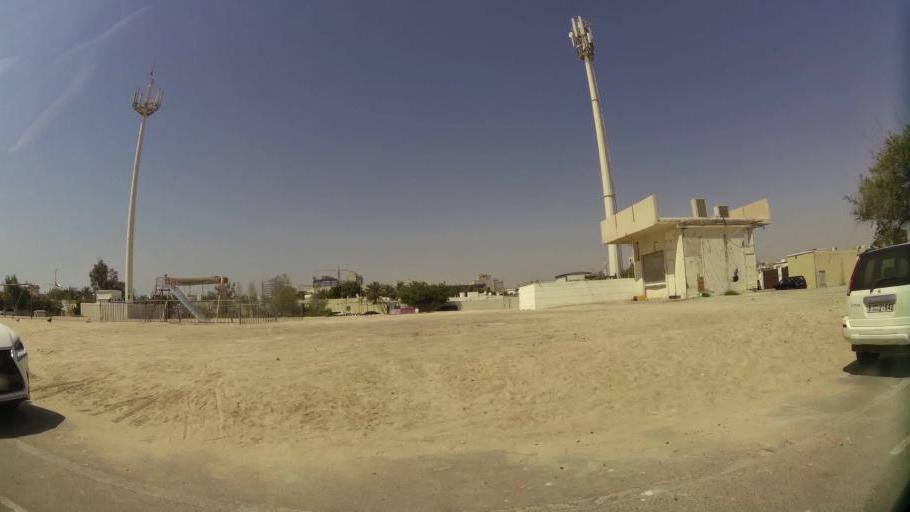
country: AE
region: Ash Shariqah
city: Sharjah
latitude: 25.2693
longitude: 55.3675
